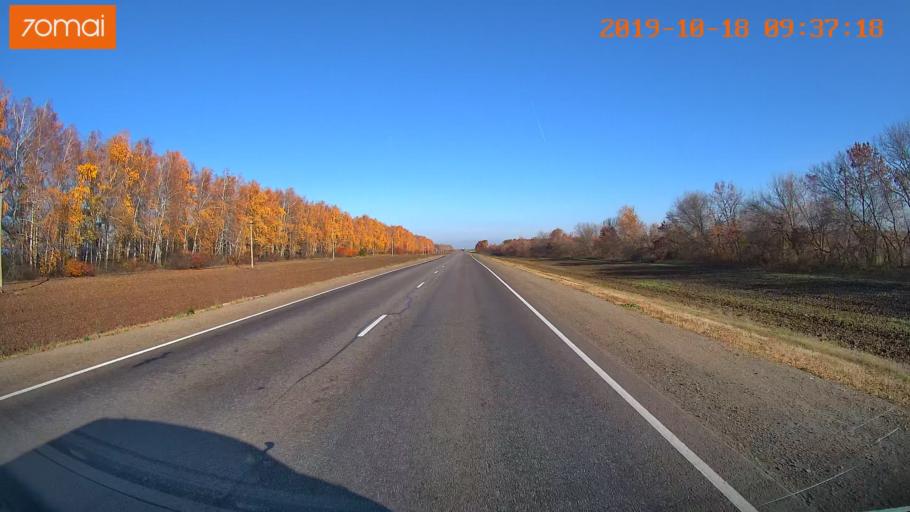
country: RU
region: Tula
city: Yefremov
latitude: 53.2199
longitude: 38.1416
